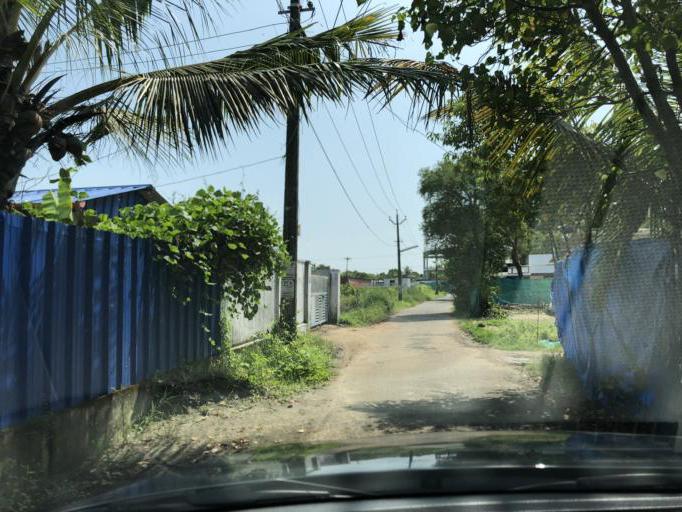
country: IN
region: Kerala
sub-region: Ernakulam
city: Cochin
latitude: 9.9920
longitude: 76.2345
